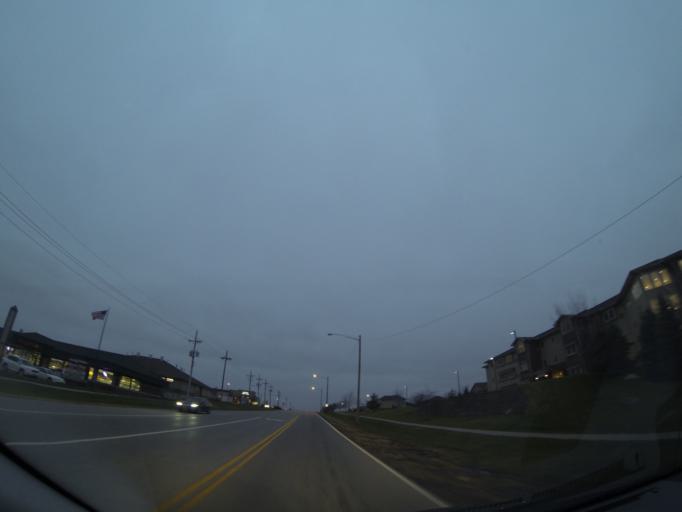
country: US
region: Nebraska
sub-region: Douglas County
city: Elkhorn
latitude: 41.2779
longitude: -96.1779
